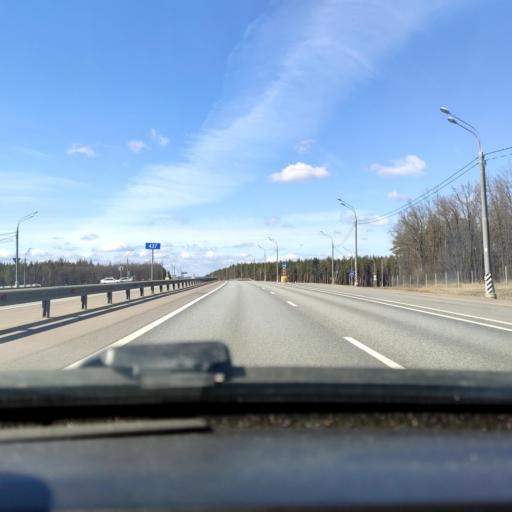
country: RU
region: Lipetsk
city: Khlevnoye
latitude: 52.3147
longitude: 39.0429
